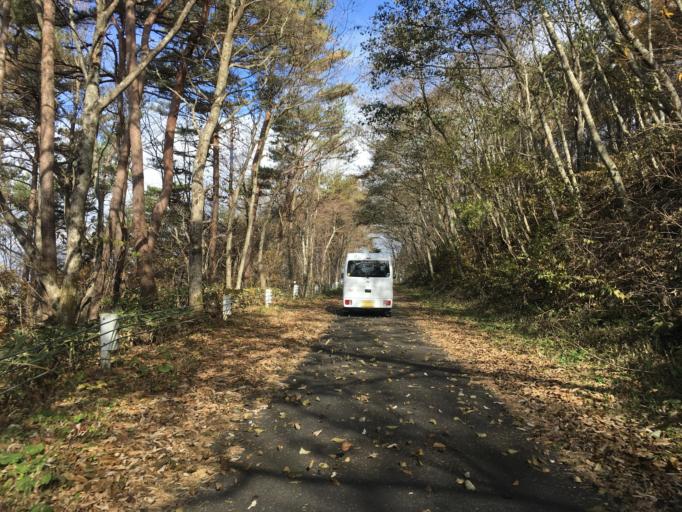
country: JP
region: Iwate
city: Mizusawa
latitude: 39.1235
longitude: 141.3021
